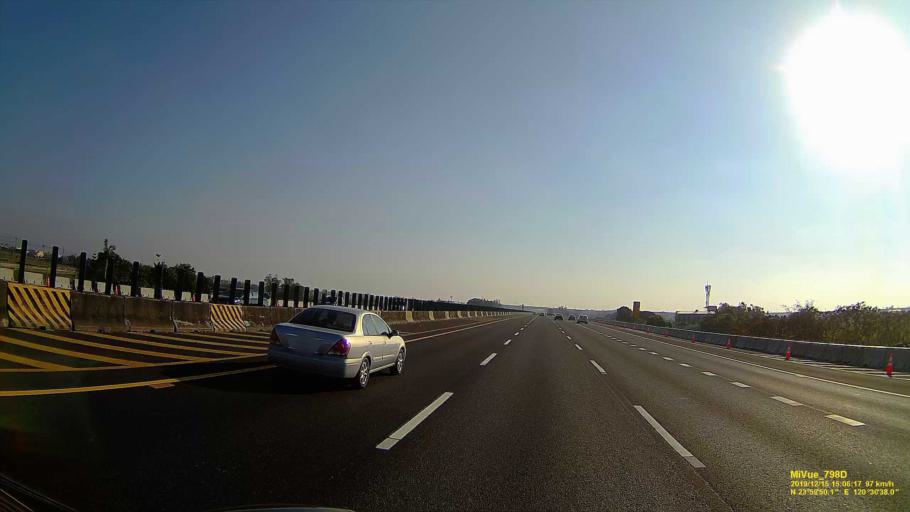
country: TW
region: Taiwan
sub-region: Changhua
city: Chang-hua
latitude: 23.9968
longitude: 120.5108
